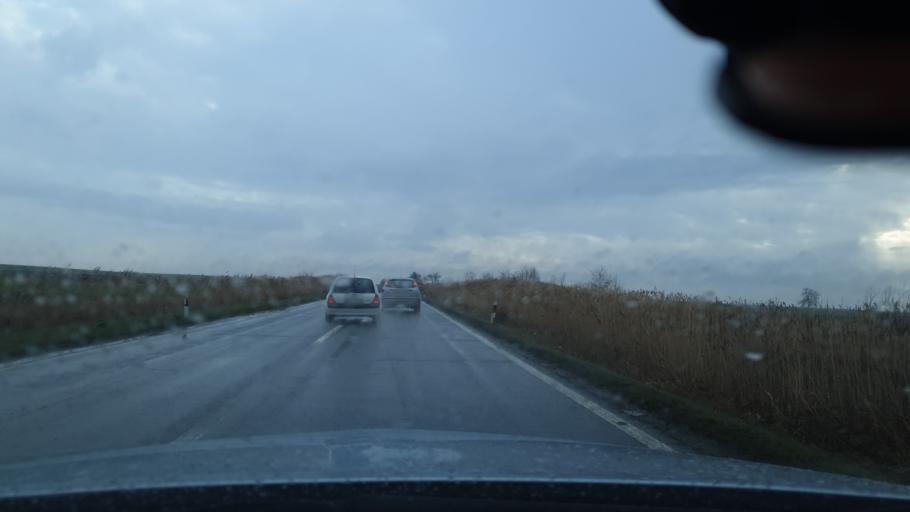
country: RS
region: Autonomna Pokrajina Vojvodina
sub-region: Juznobanatski Okrug
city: Pancevo
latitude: 44.8353
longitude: 20.8164
